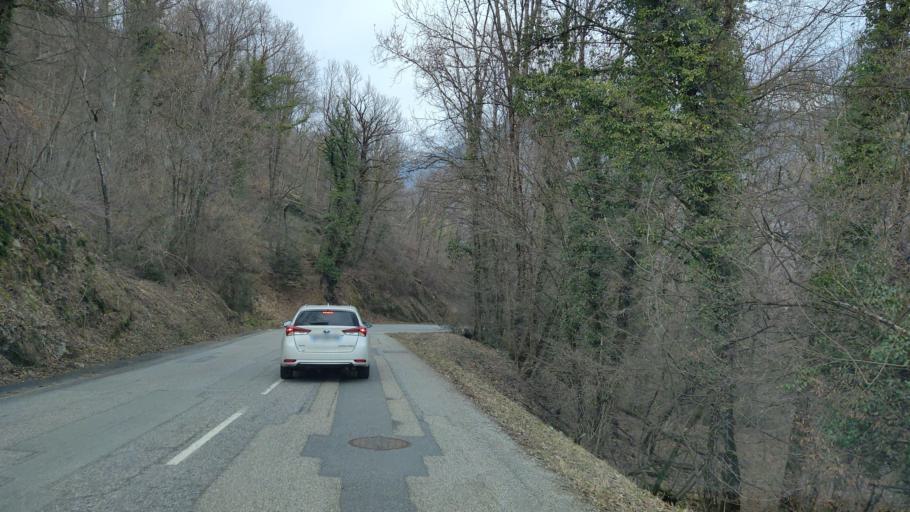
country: FR
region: Rhone-Alpes
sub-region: Departement de la Savoie
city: La Bathie
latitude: 45.6225
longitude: 6.4338
